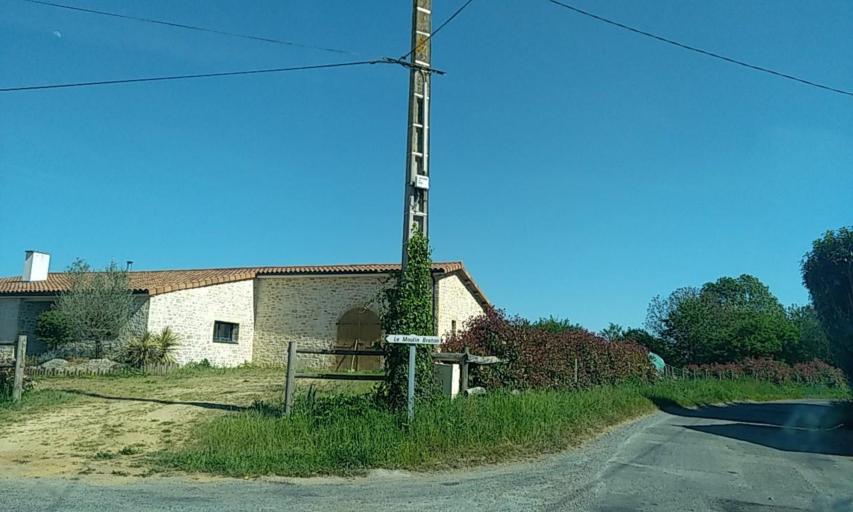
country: FR
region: Poitou-Charentes
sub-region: Departement des Deux-Sevres
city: Boisme
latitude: 46.7705
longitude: -0.4079
